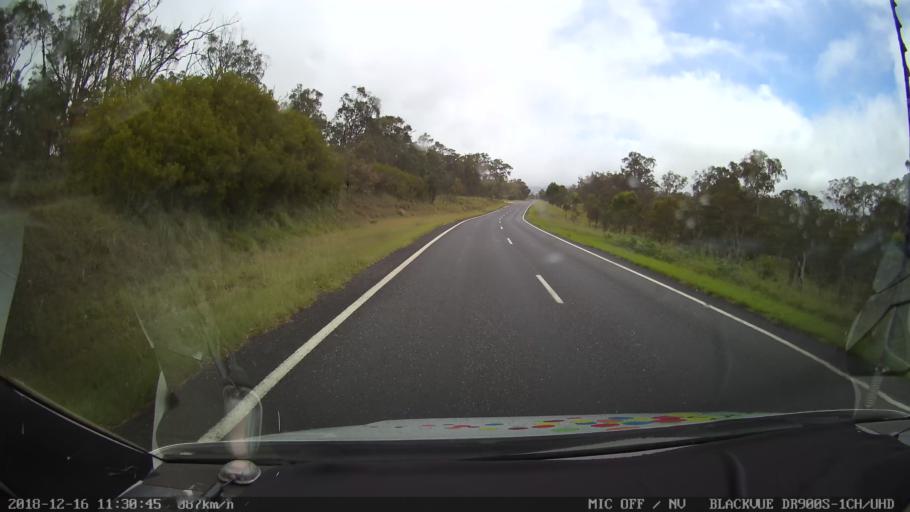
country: AU
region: New South Wales
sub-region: Tenterfield Municipality
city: Carrolls Creek
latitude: -29.0287
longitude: 152.1219
